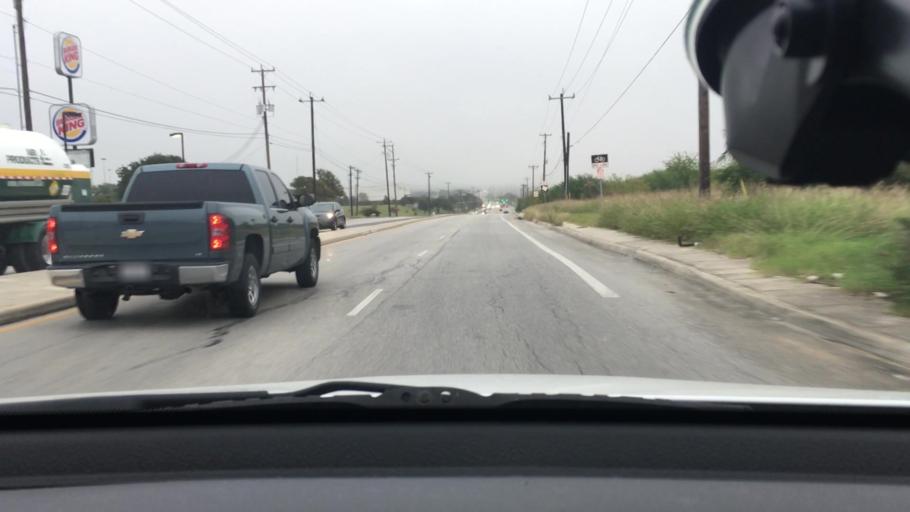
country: US
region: Texas
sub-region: Bexar County
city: Live Oak
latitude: 29.5922
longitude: -98.3510
